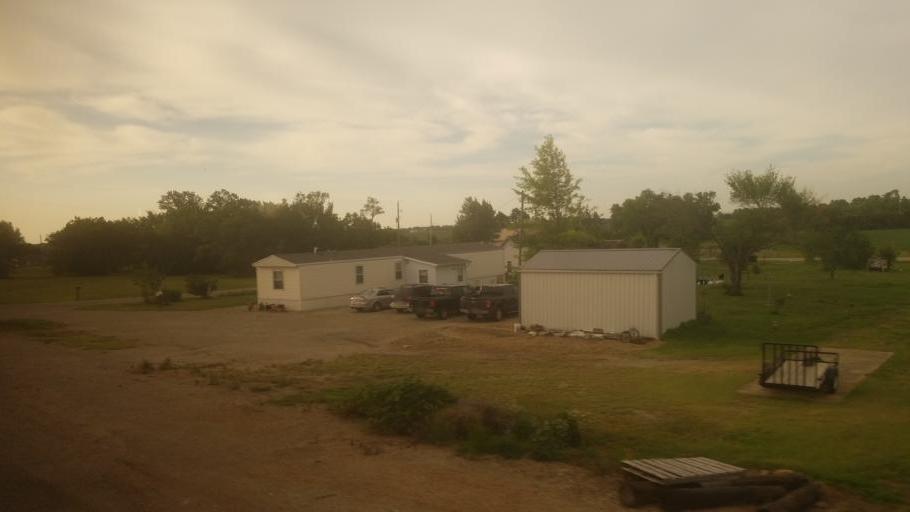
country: US
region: Kansas
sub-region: Osage County
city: Osage City
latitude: 38.5179
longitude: -95.9590
